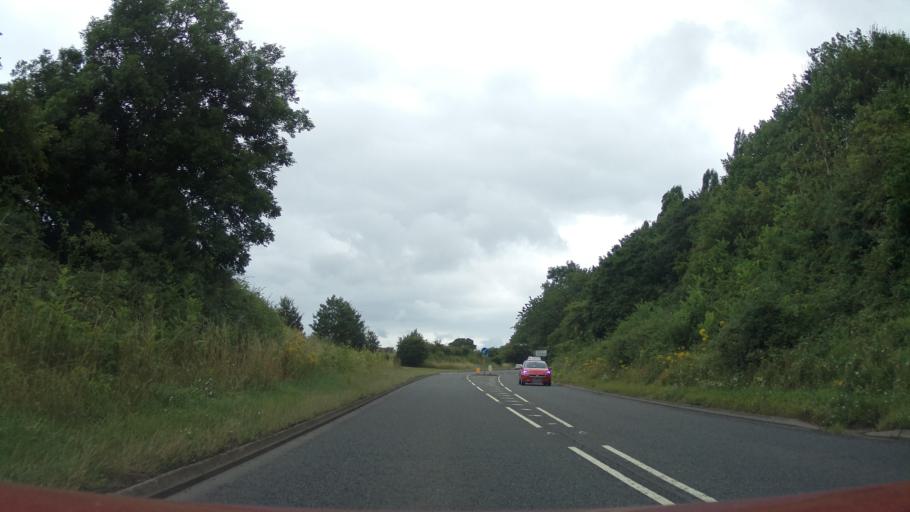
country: GB
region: England
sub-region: Worcestershire
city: Fernhill Heath
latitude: 52.2281
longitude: -2.1685
